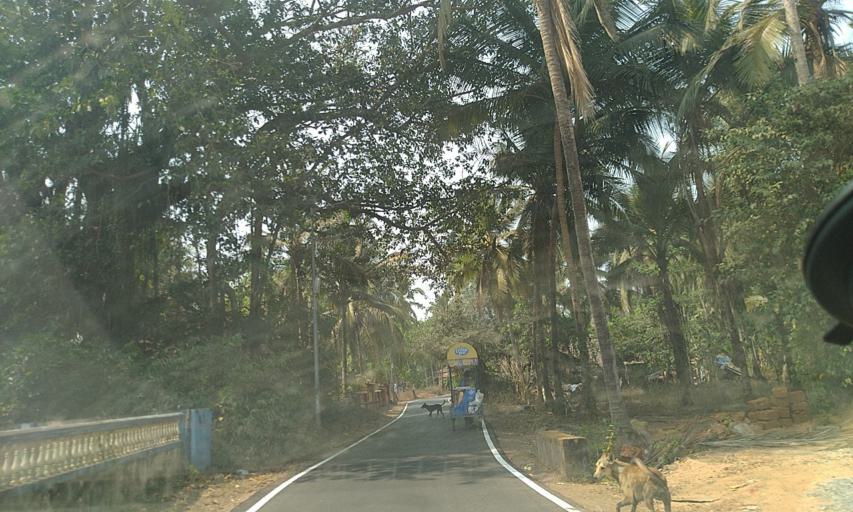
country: IN
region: Goa
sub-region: South Goa
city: Raia
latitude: 15.3024
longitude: 73.9461
